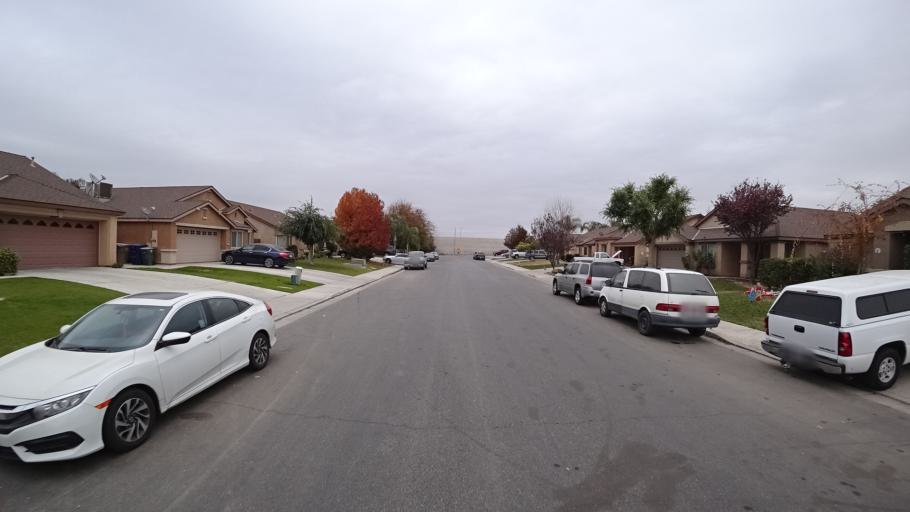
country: US
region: California
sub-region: Kern County
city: Greenfield
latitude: 35.2869
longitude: -119.0297
